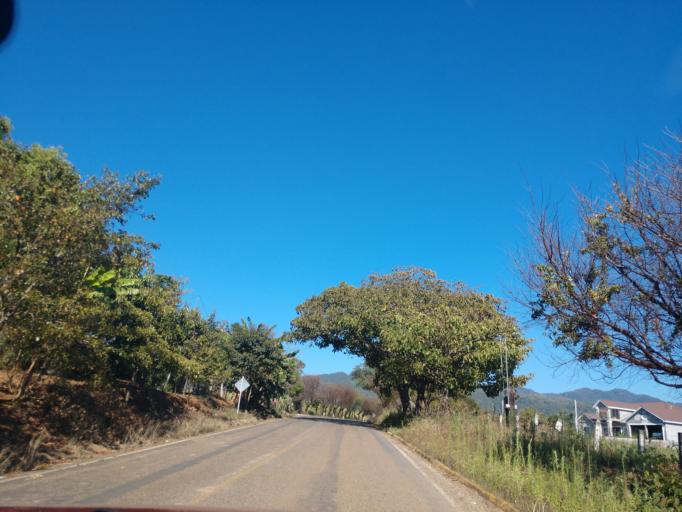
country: MX
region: Nayarit
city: Compostela
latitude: 21.2714
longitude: -104.8885
